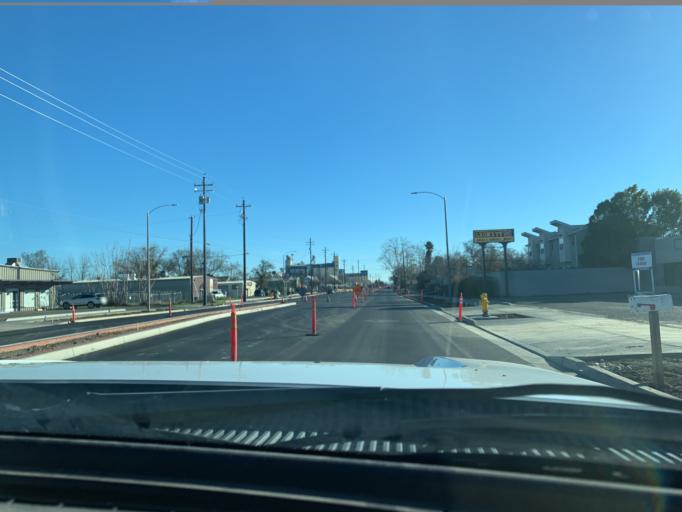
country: US
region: California
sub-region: Yolo County
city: Woodland
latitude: 38.6918
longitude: -121.7742
